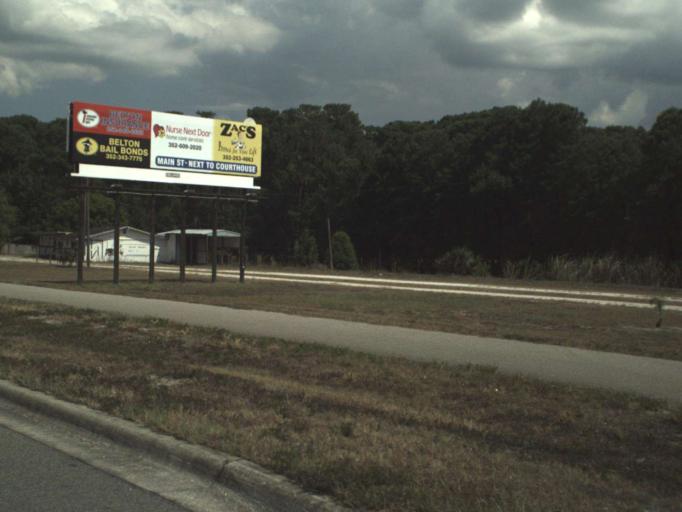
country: US
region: Florida
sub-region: Lake County
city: Tavares
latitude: 28.8111
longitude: -81.7446
